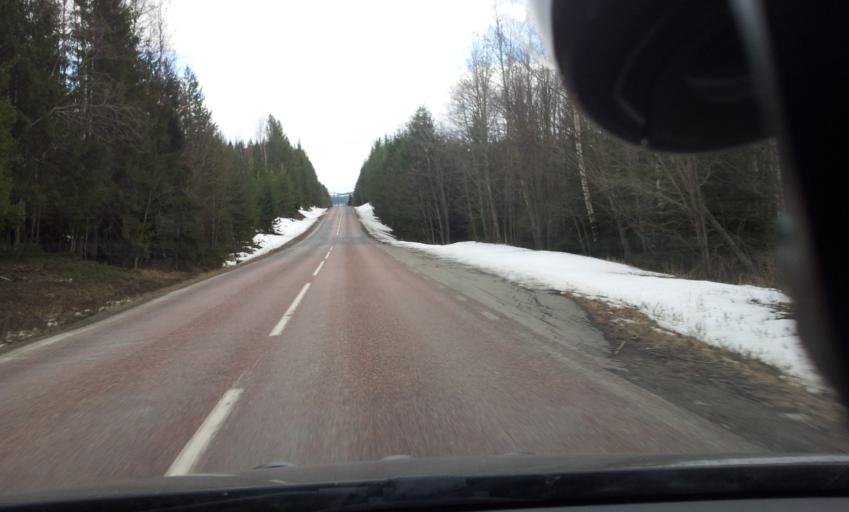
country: SE
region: Vaesternorrland
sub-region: Ange Kommun
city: Ange
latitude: 62.1456
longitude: 15.6852
